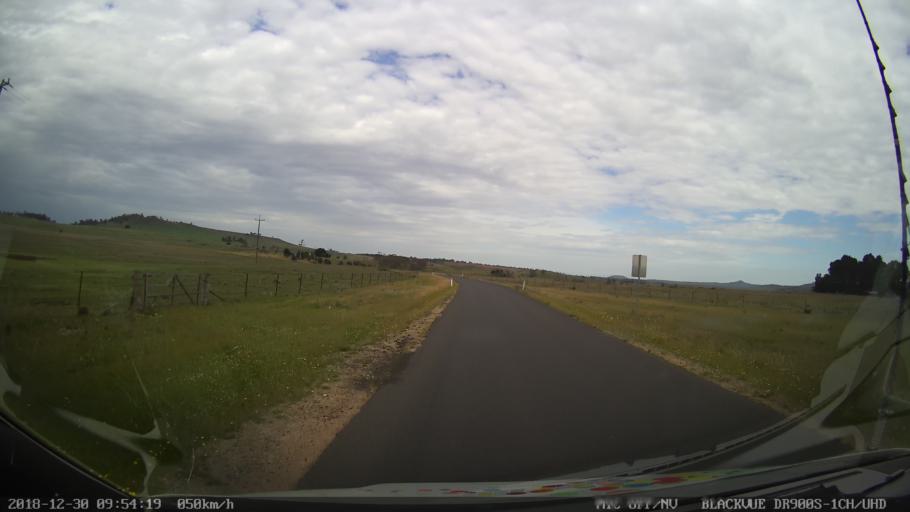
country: AU
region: New South Wales
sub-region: Cooma-Monaro
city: Cooma
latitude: -36.5184
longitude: 149.2789
